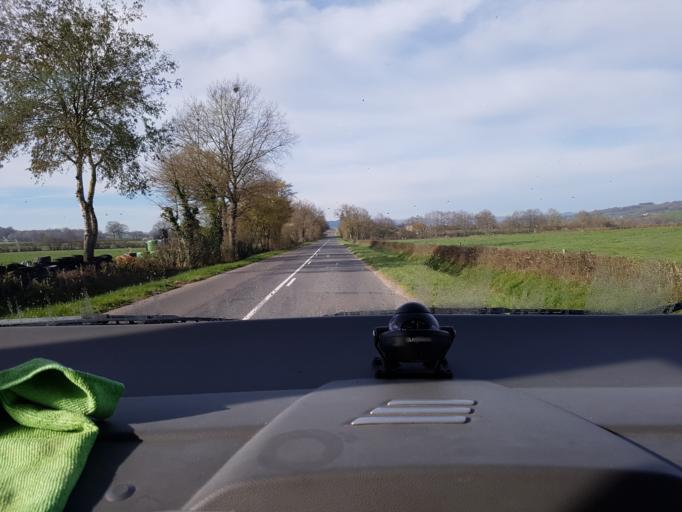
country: FR
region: Bourgogne
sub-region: Departement de Saone-et-Loire
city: Etang-sur-Arroux
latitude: 46.8241
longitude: 4.1740
